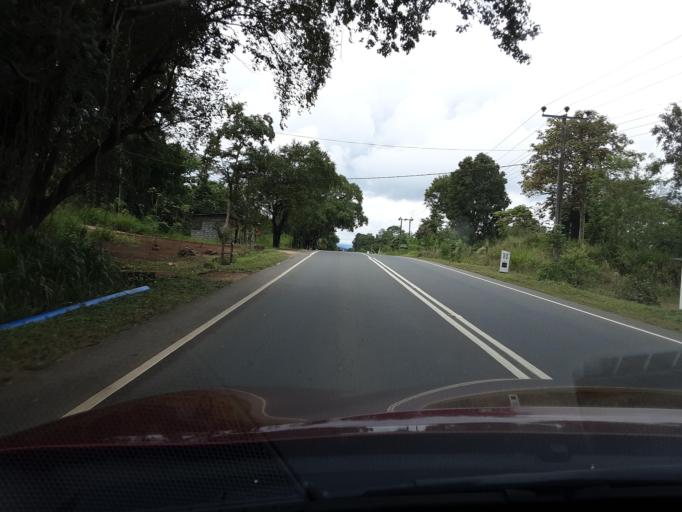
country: LK
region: Uva
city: Badulla
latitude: 7.3974
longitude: 81.1149
